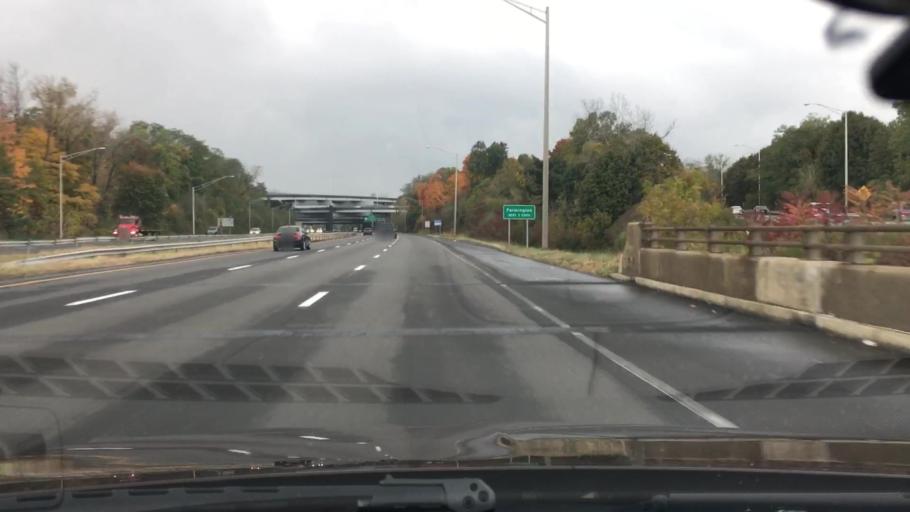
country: US
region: Connecticut
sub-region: Hartford County
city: West Hartford
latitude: 41.7246
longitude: -72.7659
